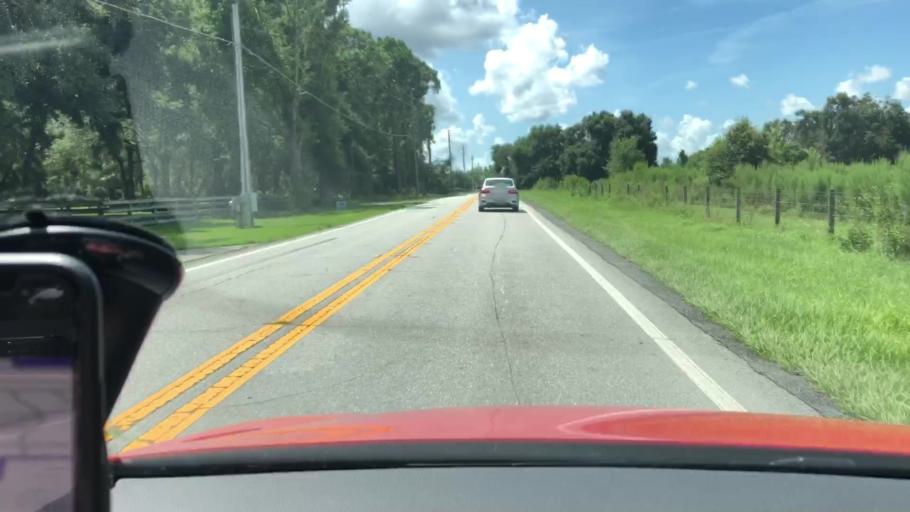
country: US
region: Florida
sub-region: Lake County
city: Eustis
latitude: 28.8373
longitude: -81.6545
